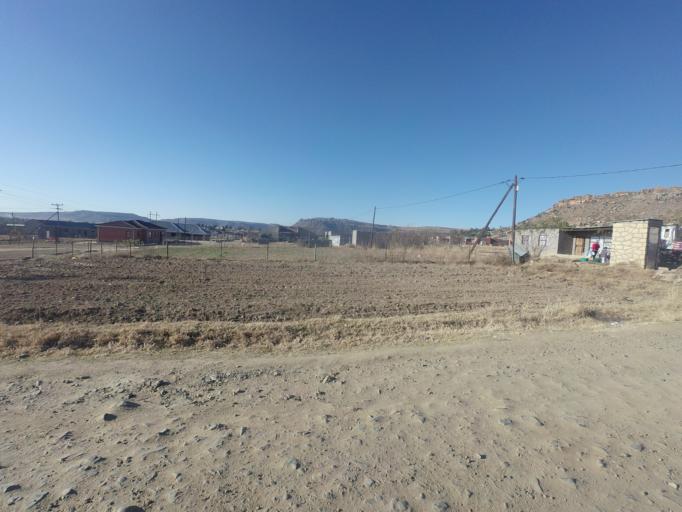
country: LS
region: Maseru
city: Maseru
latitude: -29.2998
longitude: 27.5468
